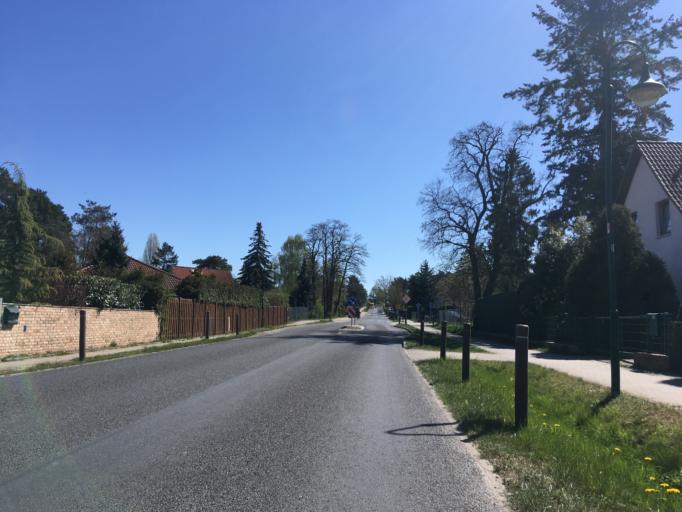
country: DE
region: Brandenburg
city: Bernau bei Berlin
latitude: 52.6462
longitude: 13.5531
